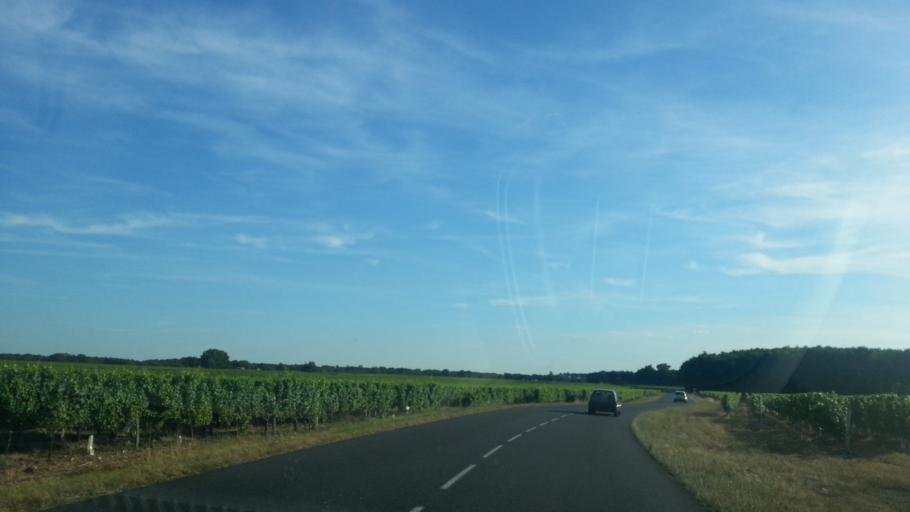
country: FR
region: Aquitaine
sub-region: Departement de la Gironde
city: Podensac
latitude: 44.6355
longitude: -0.3637
